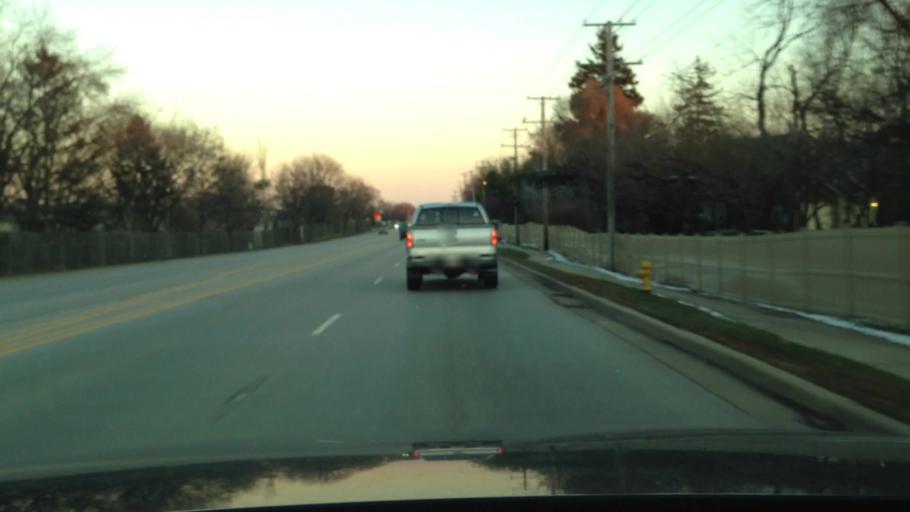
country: US
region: Illinois
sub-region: DuPage County
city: Carol Stream
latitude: 41.9412
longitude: -88.1591
